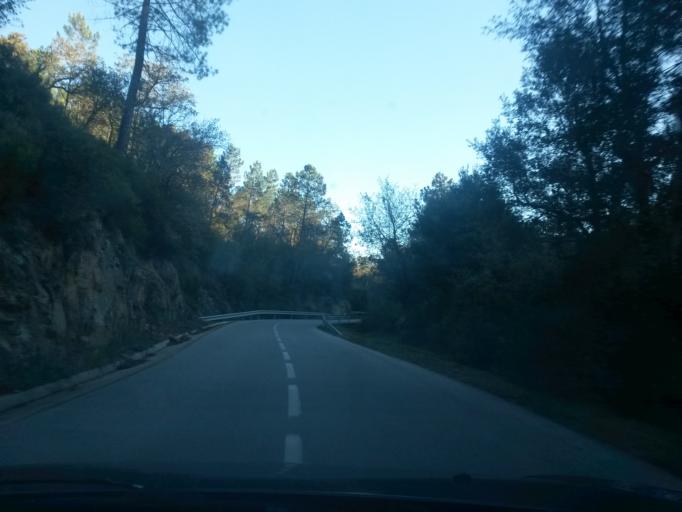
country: ES
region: Catalonia
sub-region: Provincia de Girona
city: Angles
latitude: 41.9511
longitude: 2.6803
